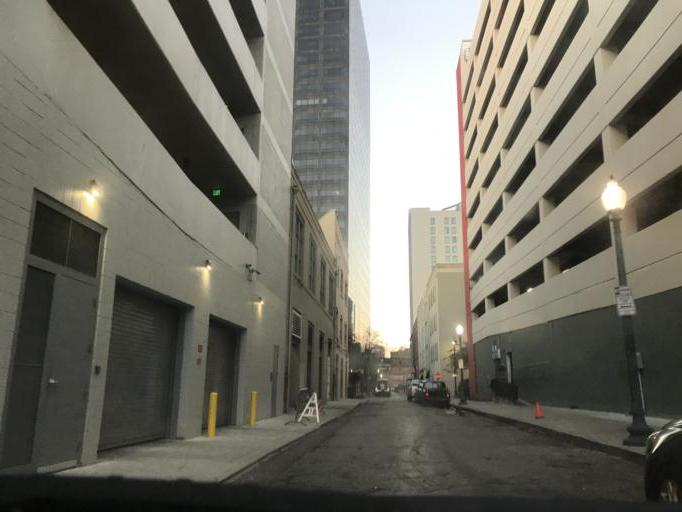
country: US
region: Louisiana
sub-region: Orleans Parish
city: New Orleans
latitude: 29.9471
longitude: -90.0680
